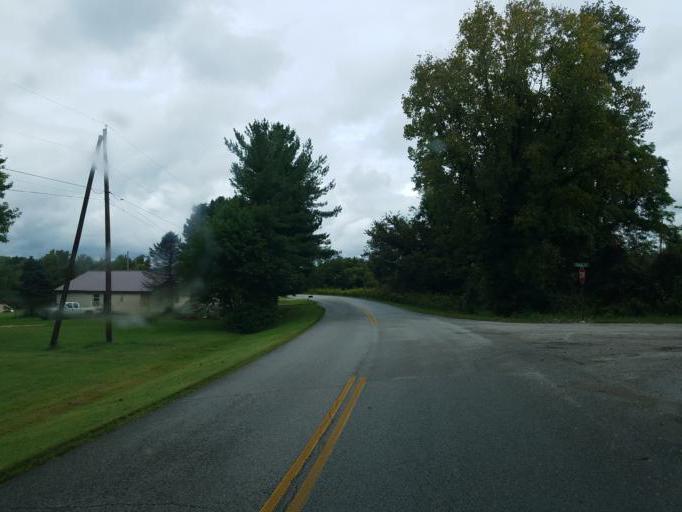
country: US
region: Ohio
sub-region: Scioto County
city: Wheelersburg
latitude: 38.7216
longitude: -82.8609
